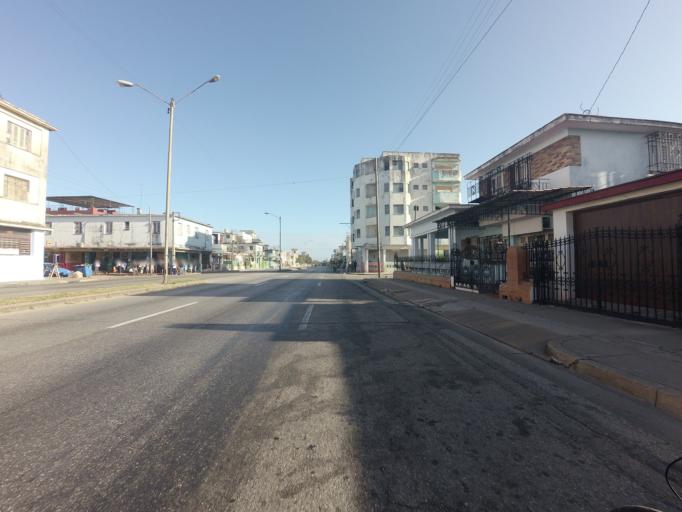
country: CU
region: La Habana
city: Cerro
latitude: 23.1092
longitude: -82.4244
